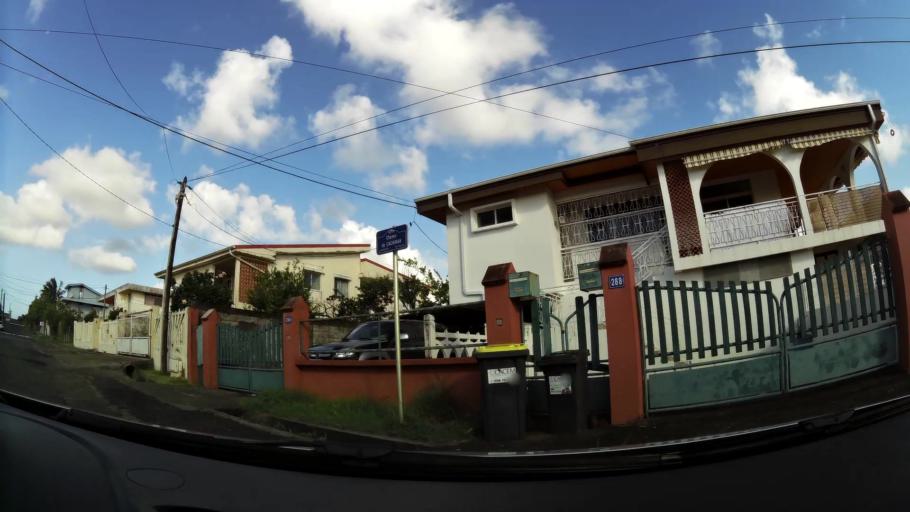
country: MQ
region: Martinique
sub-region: Martinique
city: Le Lamentin
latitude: 14.6244
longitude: -61.0133
